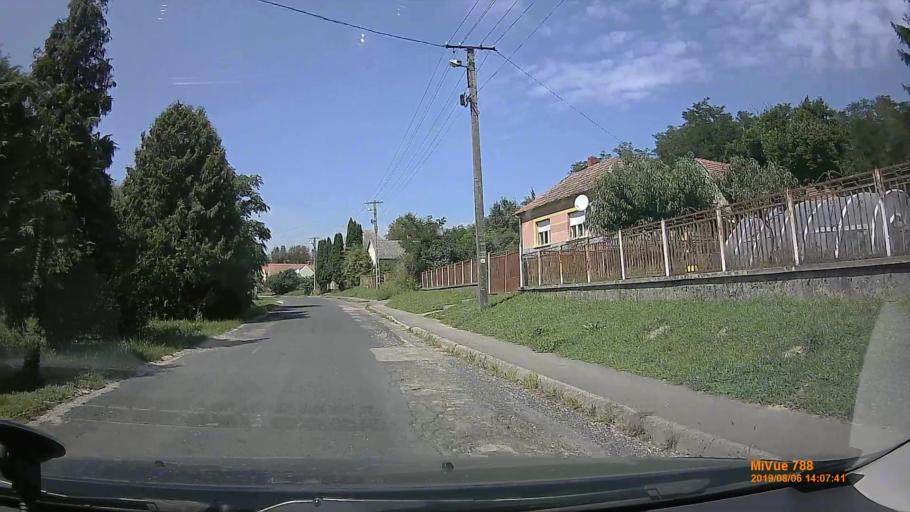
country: HU
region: Zala
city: Zalakomar
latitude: 46.5298
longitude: 17.0889
